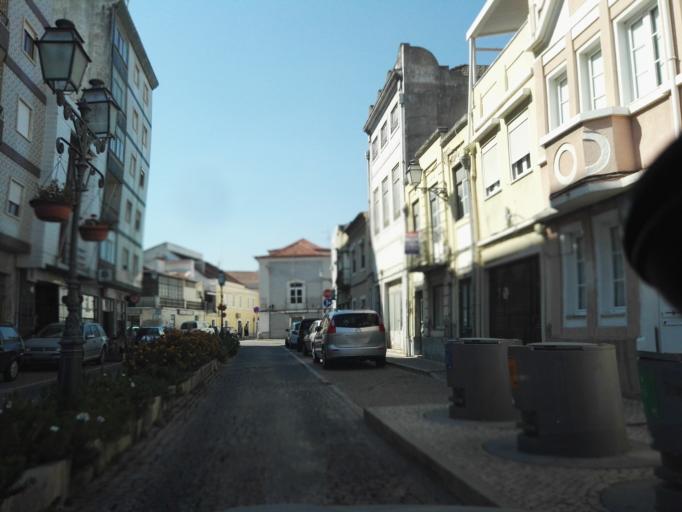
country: PT
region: Lisbon
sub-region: Vila Franca de Xira
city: Alhandra
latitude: 38.9263
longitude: -9.0077
